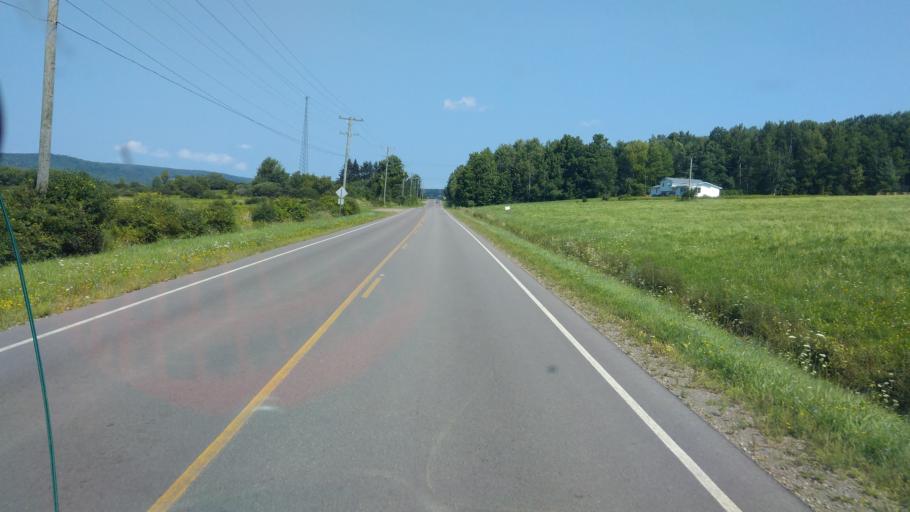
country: US
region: New York
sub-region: Allegany County
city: Belmont
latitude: 42.2910
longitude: -78.0262
